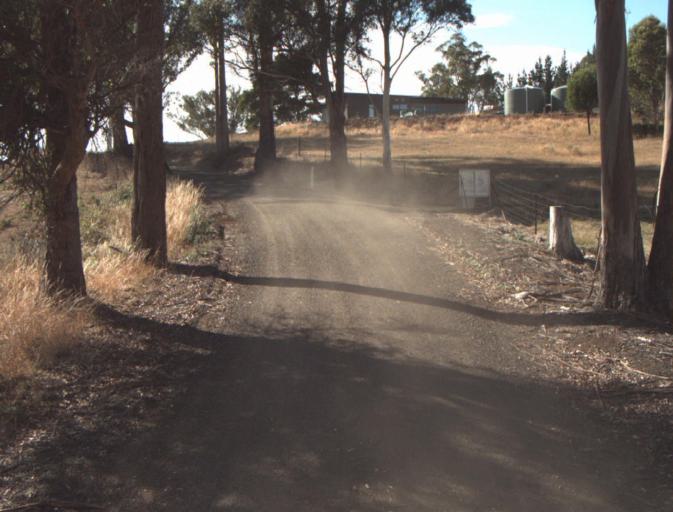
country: AU
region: Tasmania
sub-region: Dorset
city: Bridport
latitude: -41.1443
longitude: 147.2125
